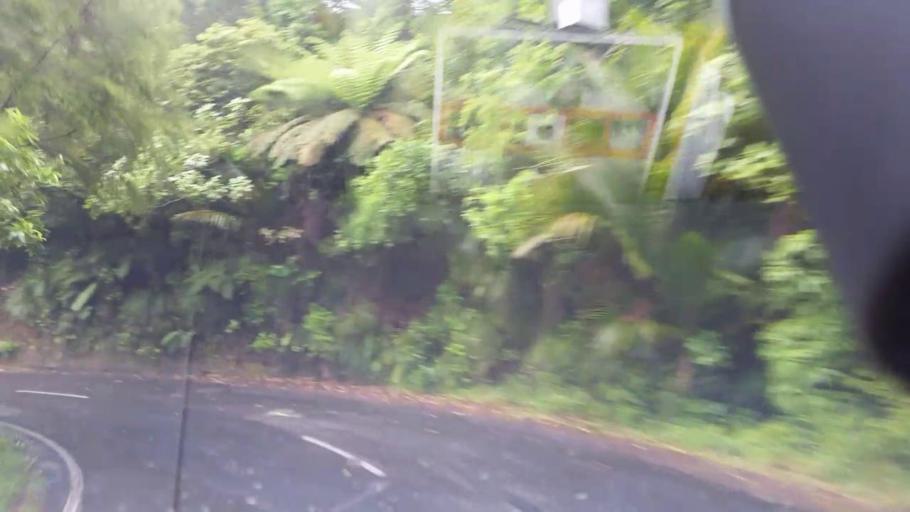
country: NZ
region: Auckland
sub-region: Auckland
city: Waitakere
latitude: -36.9096
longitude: 174.5693
